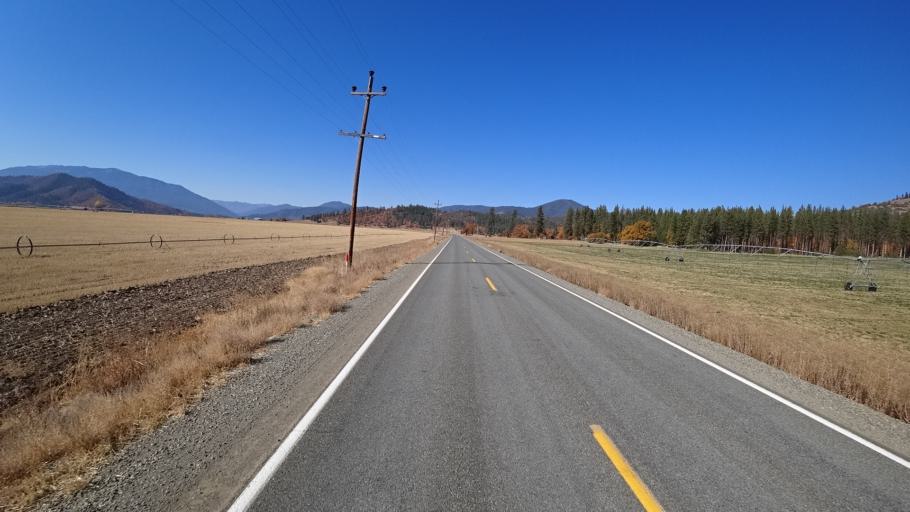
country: US
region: California
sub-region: Siskiyou County
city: Yreka
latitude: 41.6260
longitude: -122.8683
